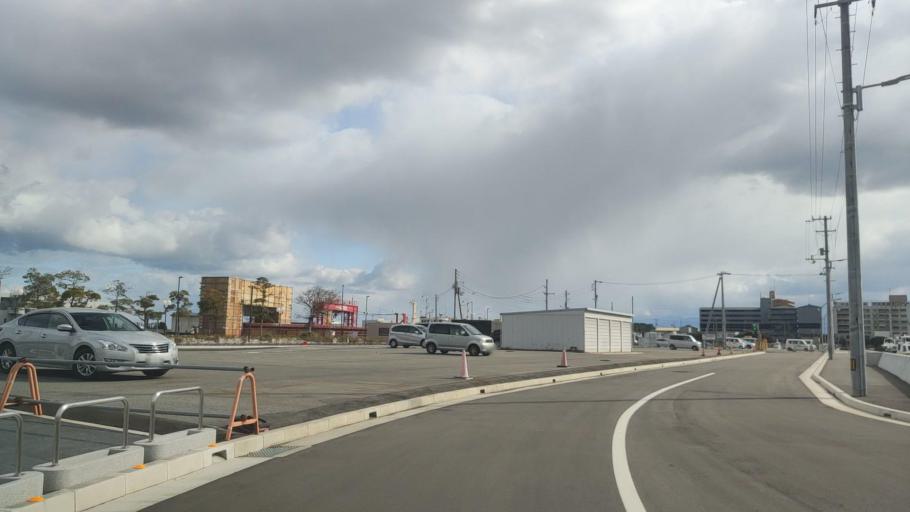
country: JP
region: Ehime
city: Saijo
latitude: 34.0689
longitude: 133.0054
